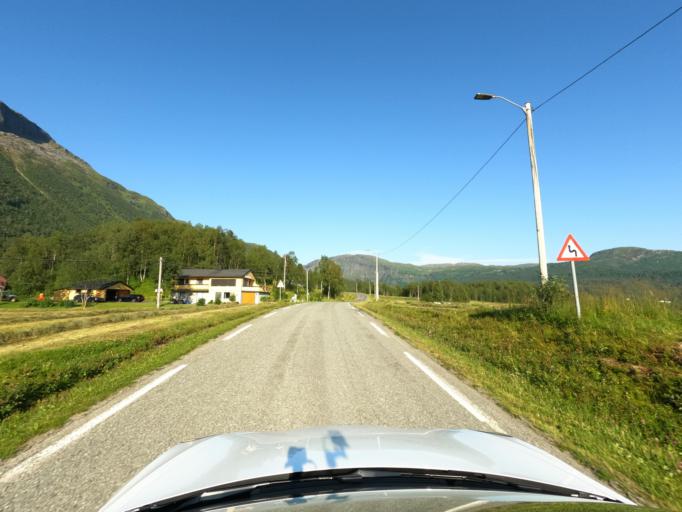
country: NO
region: Troms
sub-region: Gratangen
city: Gratangen
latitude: 68.5613
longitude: 17.6940
